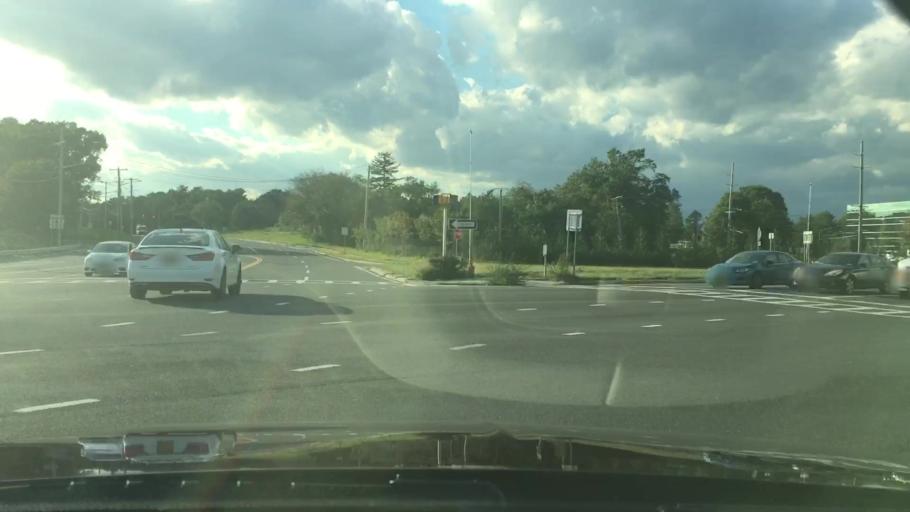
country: US
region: New York
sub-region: Suffolk County
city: Melville
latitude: 40.7669
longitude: -73.4048
